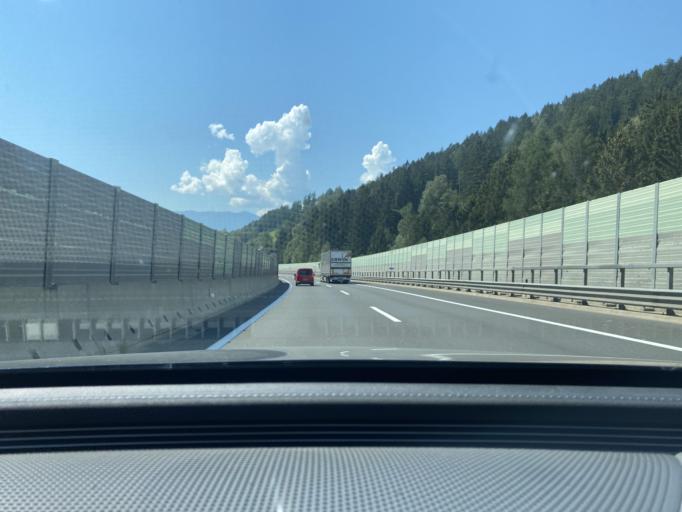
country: AT
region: Carinthia
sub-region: Politischer Bezirk Spittal an der Drau
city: Trebesing
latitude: 46.8772
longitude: 13.5064
